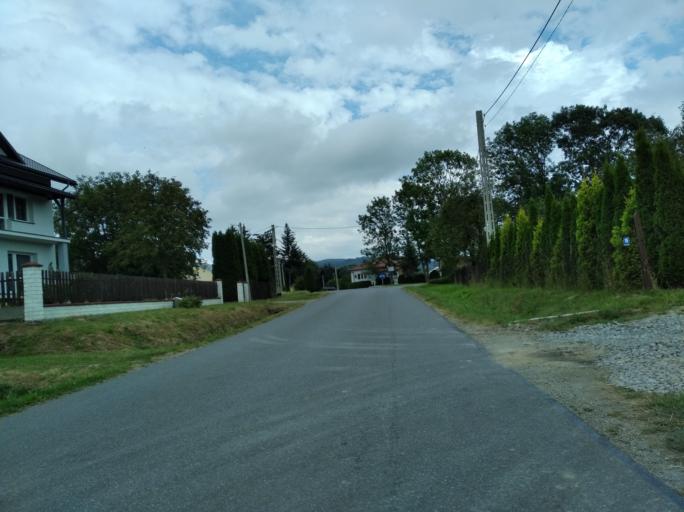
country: PL
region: Subcarpathian Voivodeship
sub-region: Powiat krosnienski
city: Odrzykon
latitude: 49.7407
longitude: 21.7375
